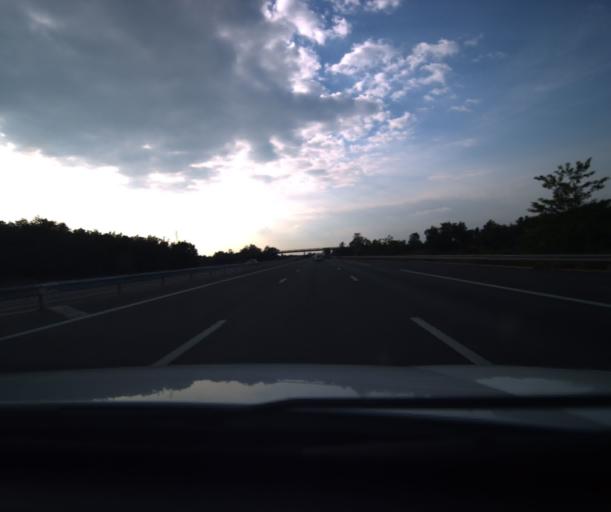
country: FR
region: Midi-Pyrenees
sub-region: Departement du Tarn-et-Garonne
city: Pompignan
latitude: 43.8375
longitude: 1.3338
